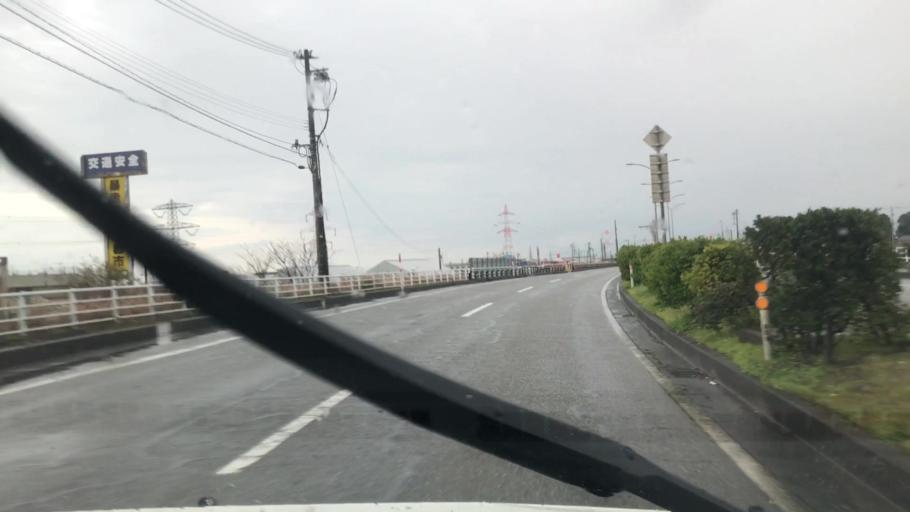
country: JP
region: Toyama
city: Toyama-shi
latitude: 36.6281
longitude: 137.2056
